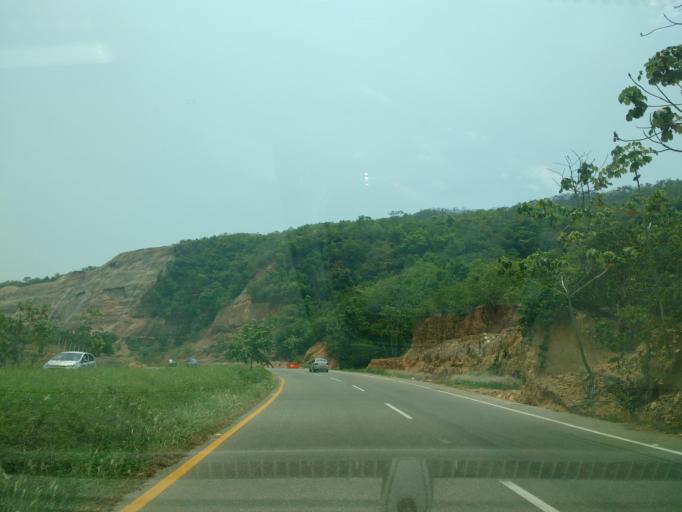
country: CO
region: Tolima
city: Melgar
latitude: 4.2255
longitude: -74.6305
